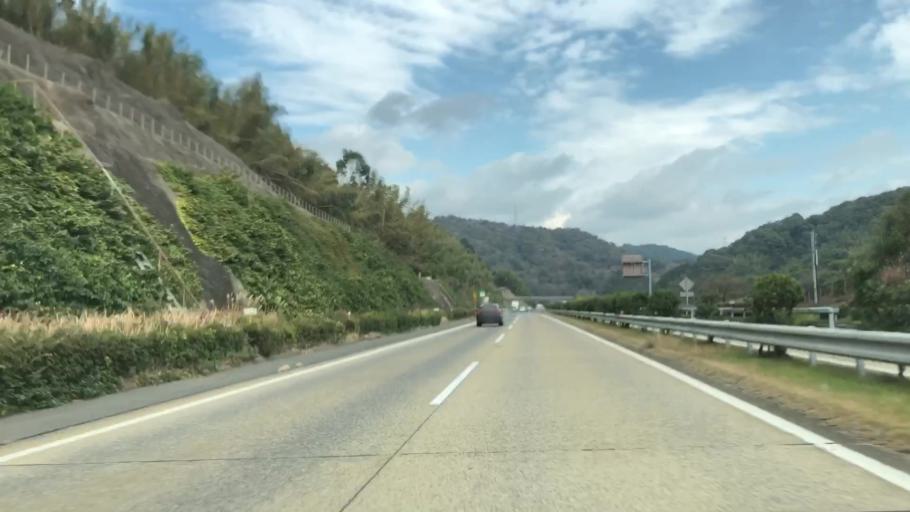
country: JP
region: Saga Prefecture
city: Kanzakimachi-kanzaki
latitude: 33.3344
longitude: 130.3252
